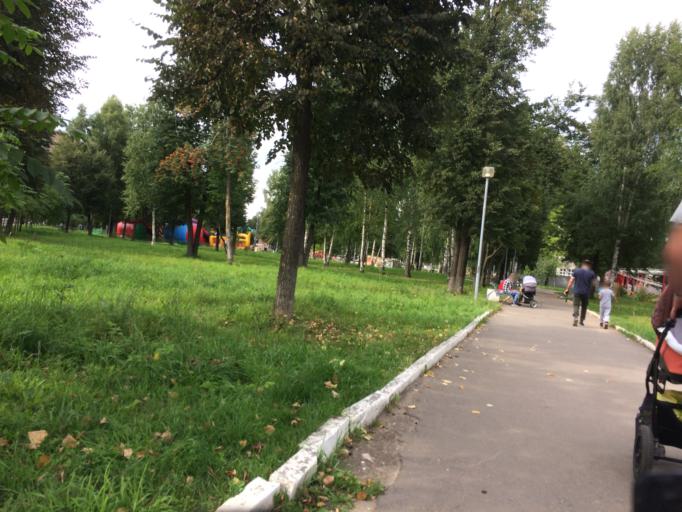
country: RU
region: Mariy-El
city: Yoshkar-Ola
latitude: 56.6383
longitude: 47.8674
